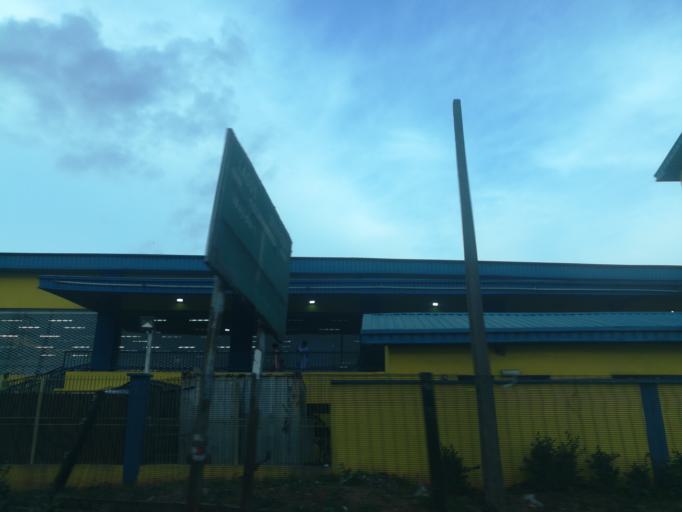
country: NG
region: Lagos
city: Ebute Ikorodu
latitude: 6.6185
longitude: 3.4753
